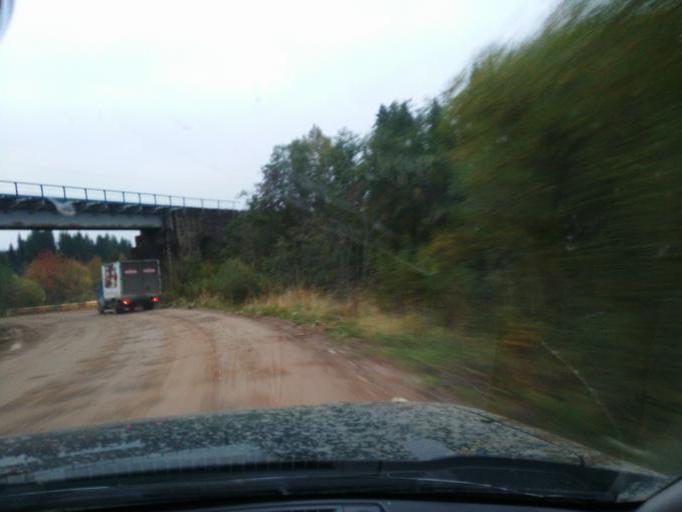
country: RU
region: Sverdlovsk
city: Sylva
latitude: 57.7984
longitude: 58.5375
